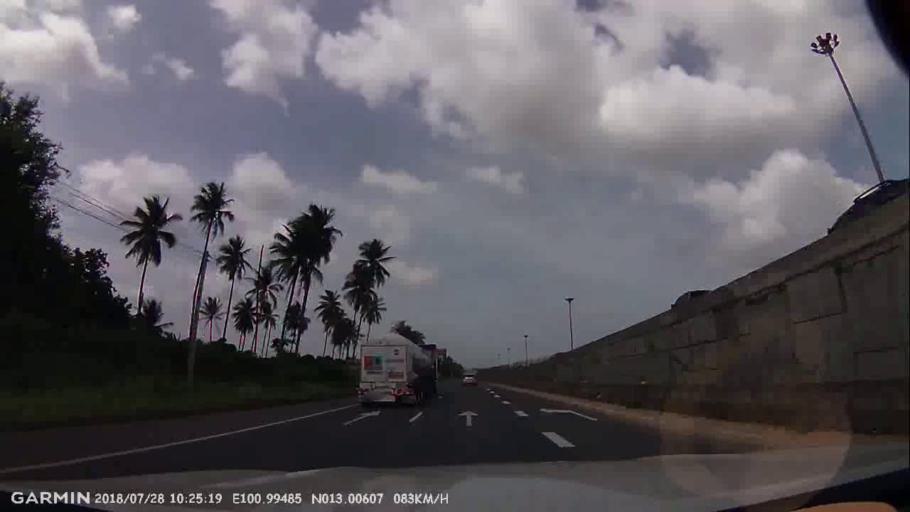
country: TH
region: Chon Buri
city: Ban Talat Bueng
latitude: 13.0059
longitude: 100.9948
